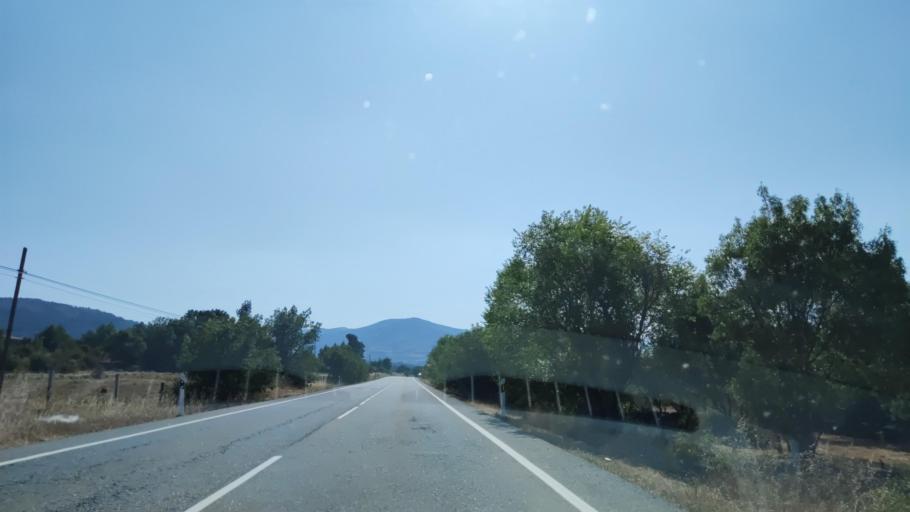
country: ES
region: Madrid
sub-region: Provincia de Madrid
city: Garganta de los Montes
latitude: 40.9433
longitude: -3.6911
